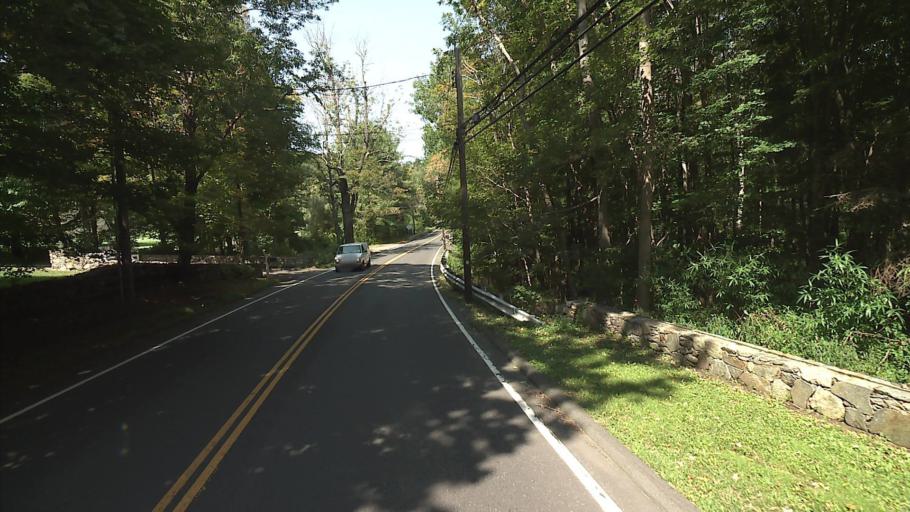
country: US
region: Connecticut
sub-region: Fairfield County
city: Georgetown
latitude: 41.2688
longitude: -73.3324
